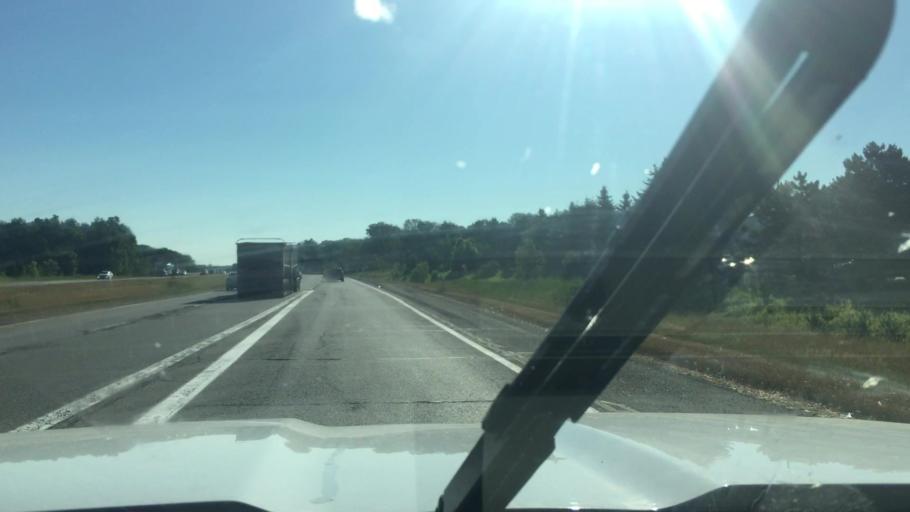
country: US
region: Michigan
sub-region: Ottawa County
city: Hudsonville
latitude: 42.8499
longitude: -85.8553
